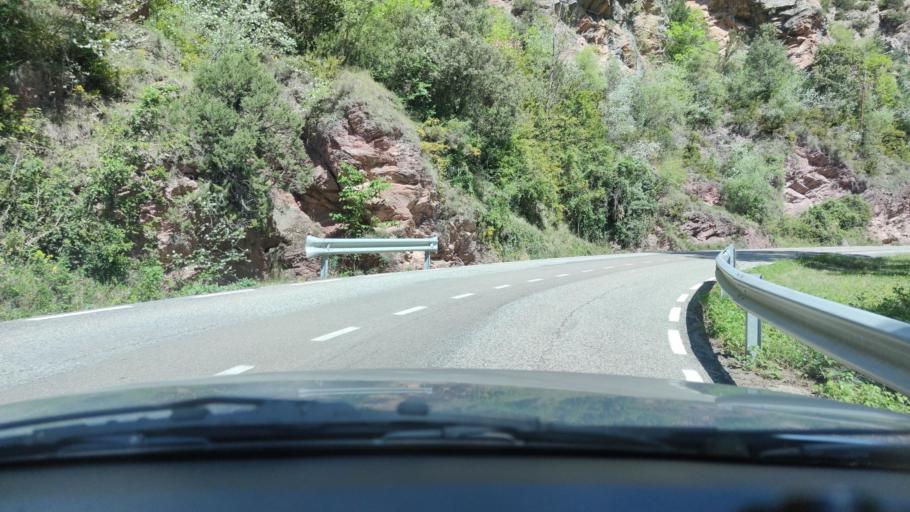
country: ES
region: Catalonia
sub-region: Provincia de Lleida
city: Coll de Nargo
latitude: 42.3072
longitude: 1.2885
